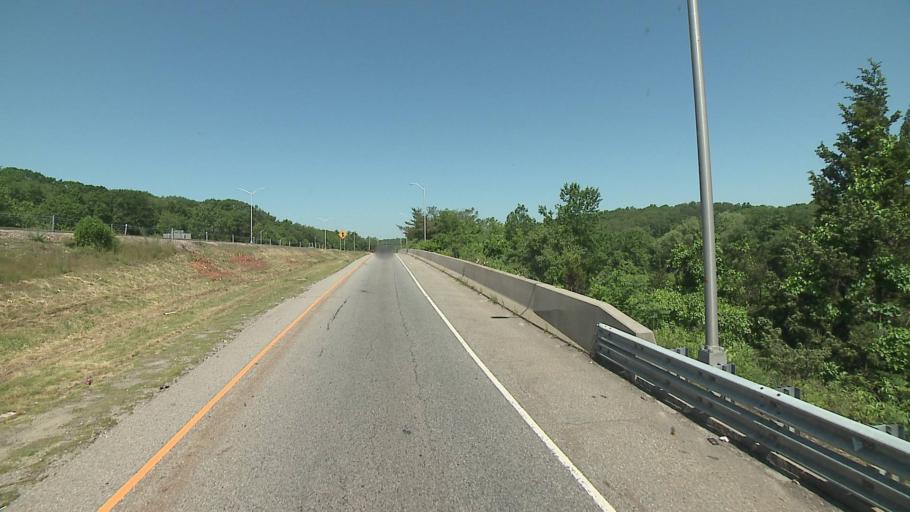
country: US
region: Connecticut
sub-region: New London County
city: Oxoboxo River
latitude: 41.4837
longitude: -72.1008
